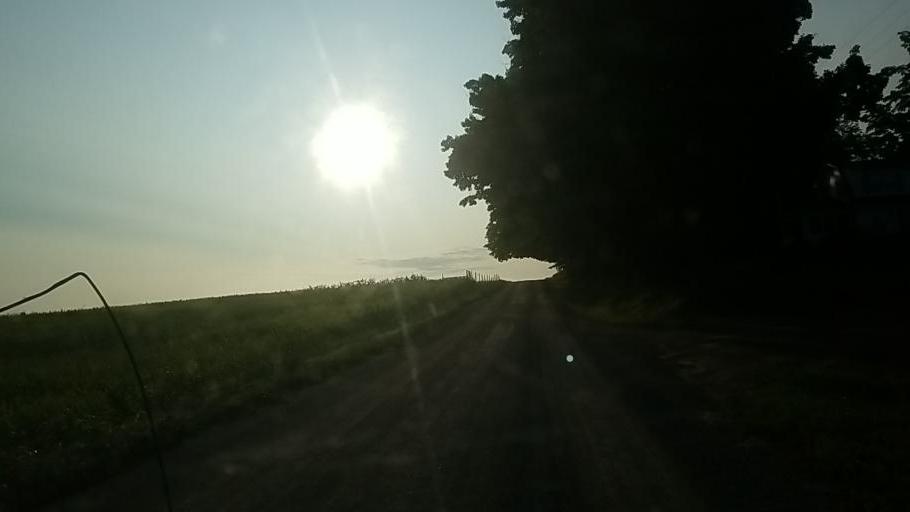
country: US
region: Michigan
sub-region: Newaygo County
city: Fremont
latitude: 43.4529
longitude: -86.0302
